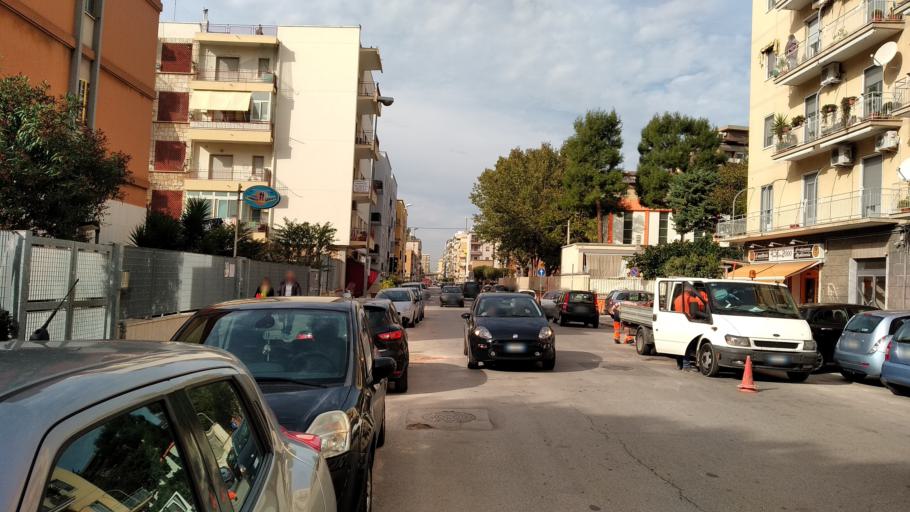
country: IT
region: Apulia
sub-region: Provincia di Bari
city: Bari
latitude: 41.1140
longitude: 16.8959
